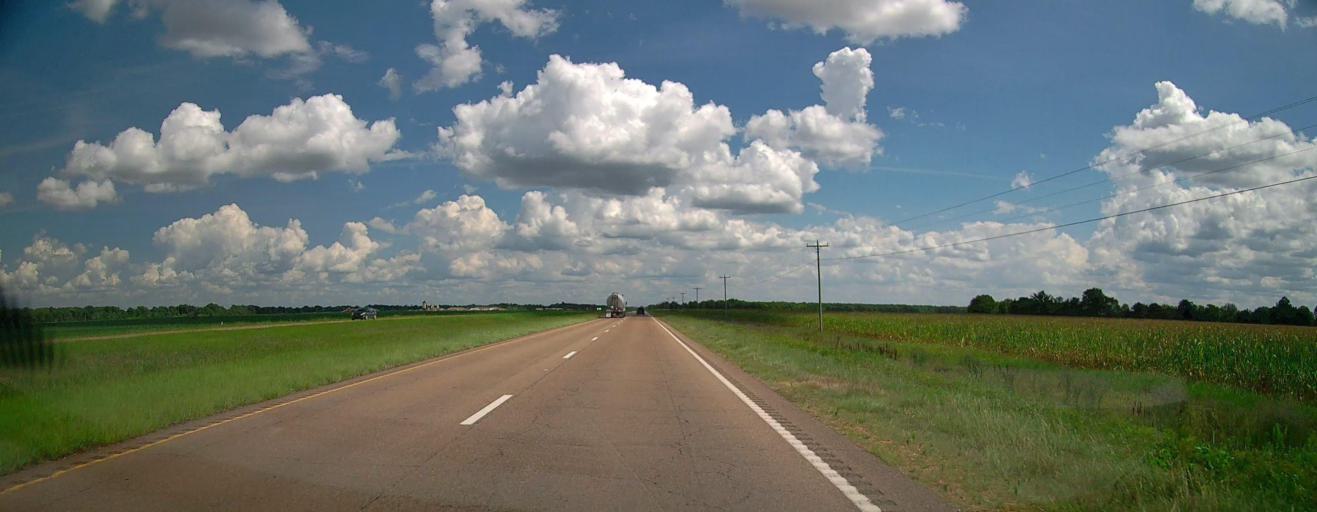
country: US
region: Mississippi
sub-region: Lowndes County
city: Columbus Air Force Base
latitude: 33.7097
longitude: -88.4498
